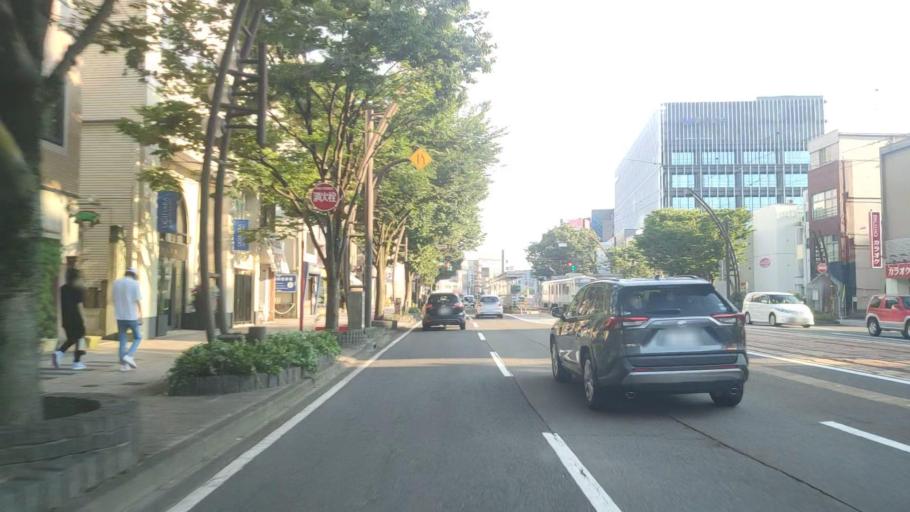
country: JP
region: Fukui
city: Fukui-shi
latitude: 36.0645
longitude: 136.2178
